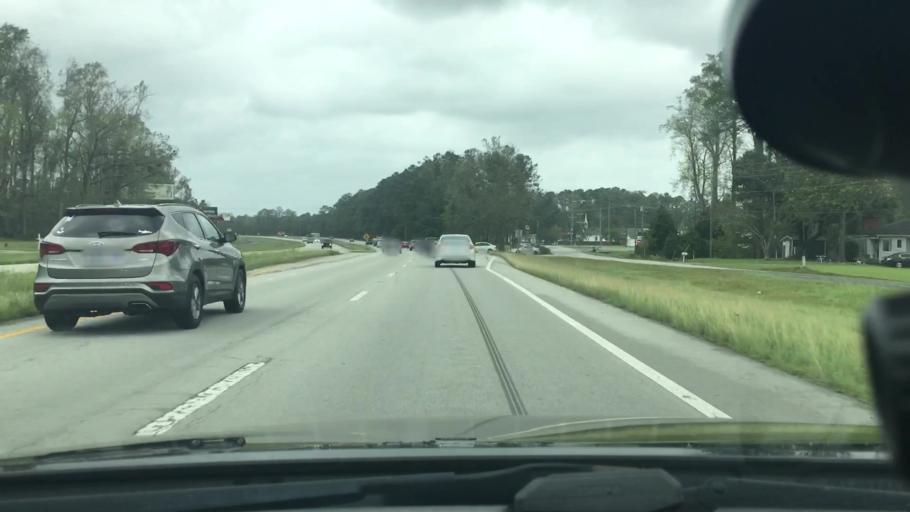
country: US
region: North Carolina
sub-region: Craven County
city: Neuse Forest
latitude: 34.9529
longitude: -76.9489
